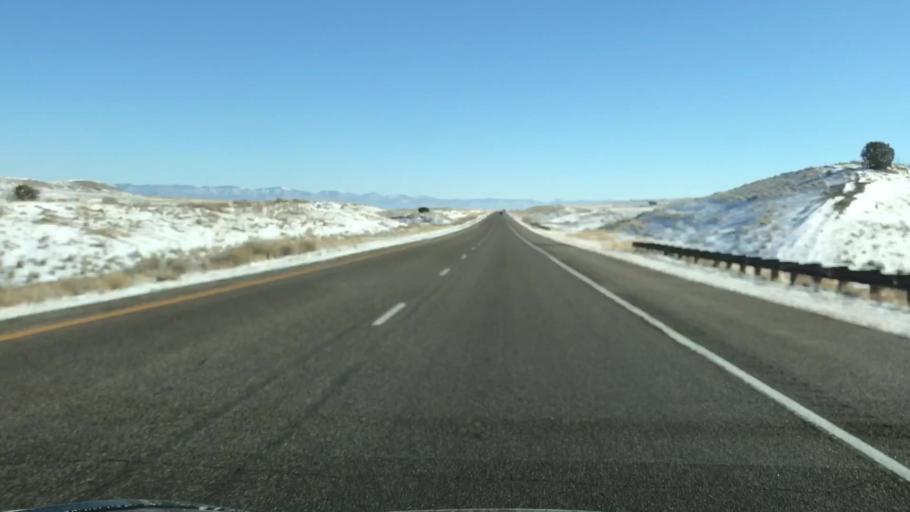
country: US
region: Colorado
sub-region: Mesa County
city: Loma
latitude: 39.2222
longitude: -108.9440
